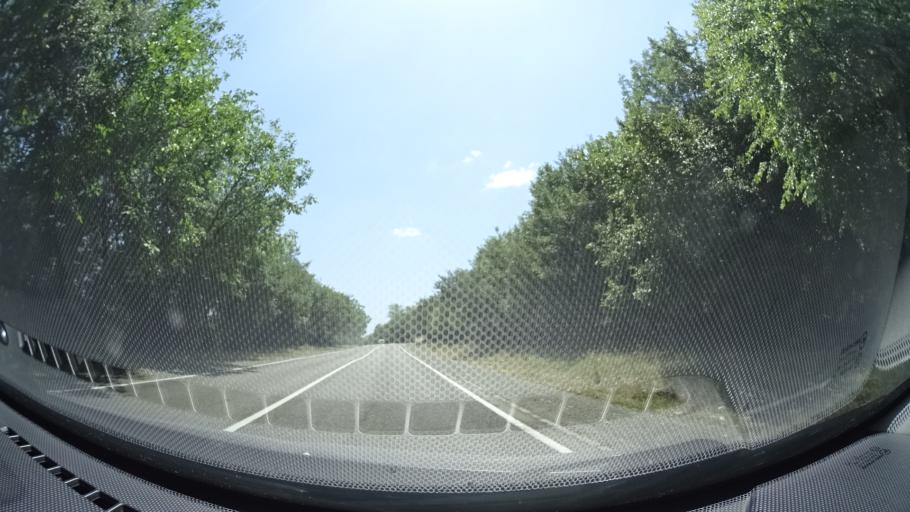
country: GE
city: Zhinvali
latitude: 42.0361
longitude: 44.7455
